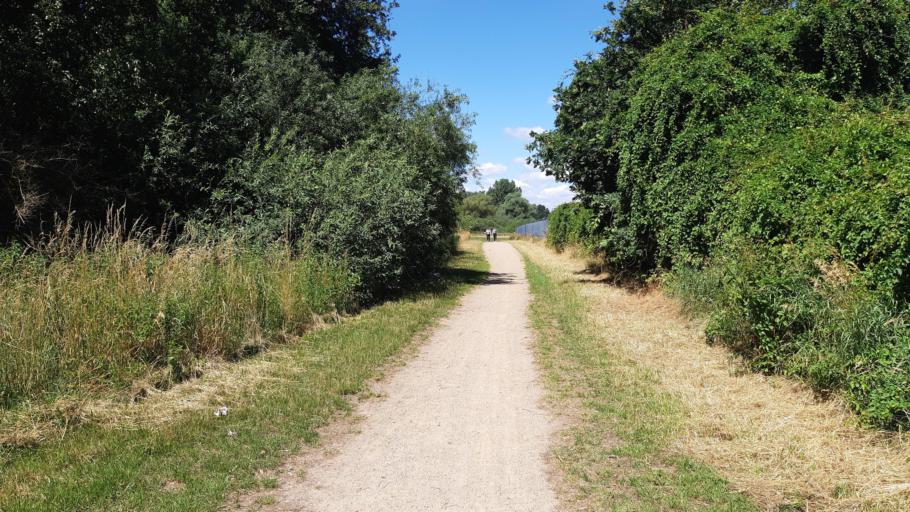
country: DE
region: Lower Saxony
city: Dahlenburg
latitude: 53.1901
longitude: 10.7417
